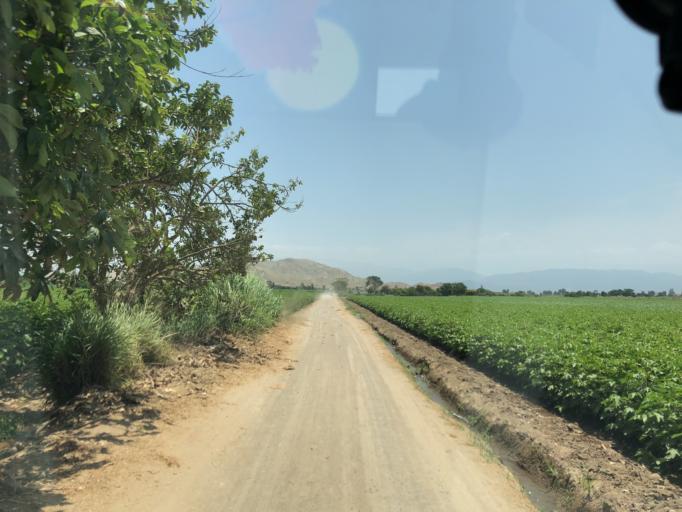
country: PE
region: Lima
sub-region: Provincia de Canete
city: Quilmana
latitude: -12.9754
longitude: -76.4248
